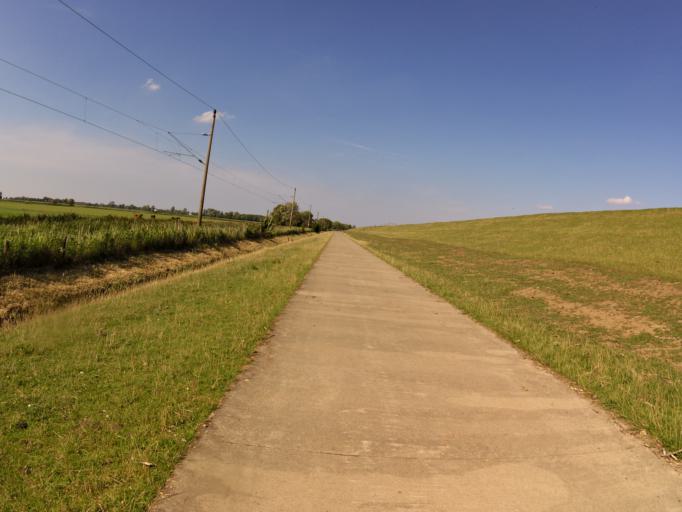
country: DE
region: Lower Saxony
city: Nordenham
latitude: 53.4506
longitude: 8.4754
